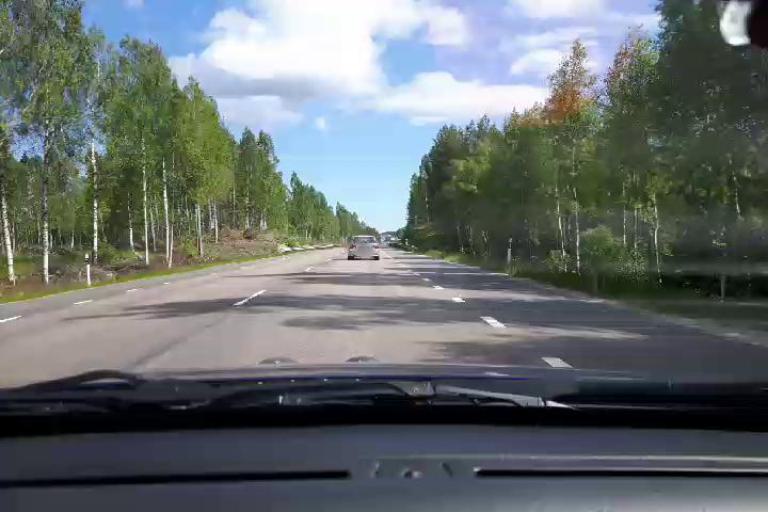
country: SE
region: Gaevleborg
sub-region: Hudiksvalls Kommun
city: Sorforsa
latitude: 61.7192
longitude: 17.0244
